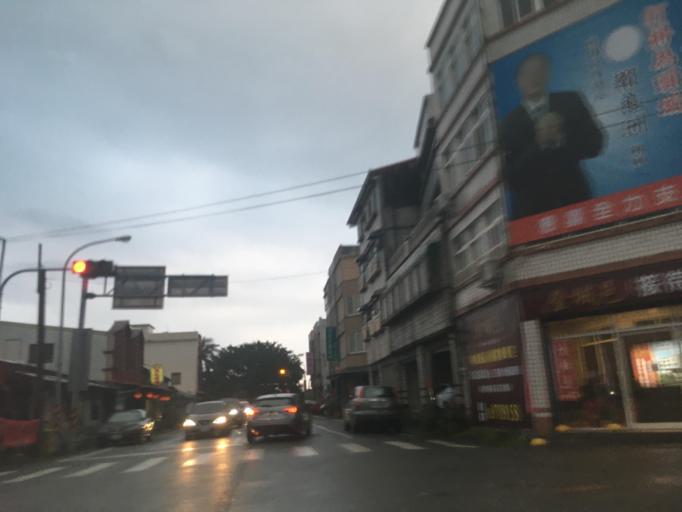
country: TW
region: Taiwan
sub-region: Yilan
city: Yilan
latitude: 24.8544
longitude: 121.8226
